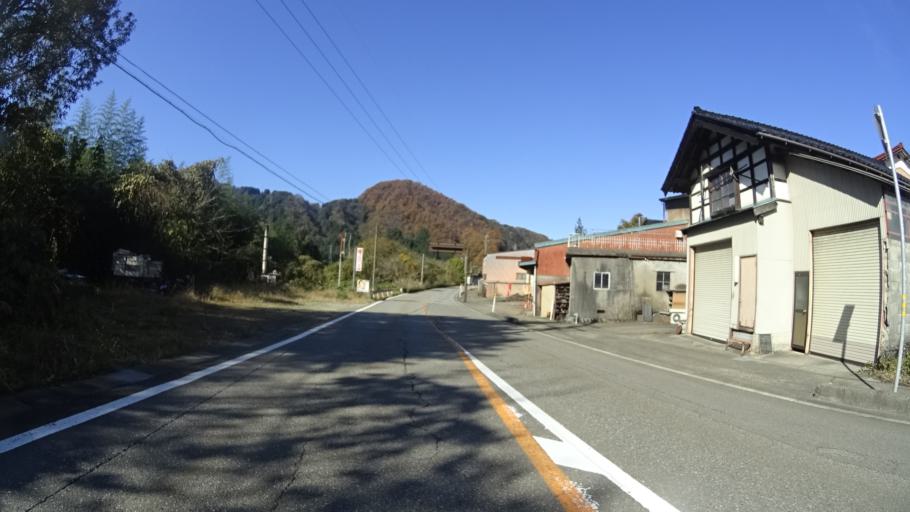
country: JP
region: Ishikawa
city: Tsurugi-asahimachi
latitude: 36.3450
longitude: 136.6307
